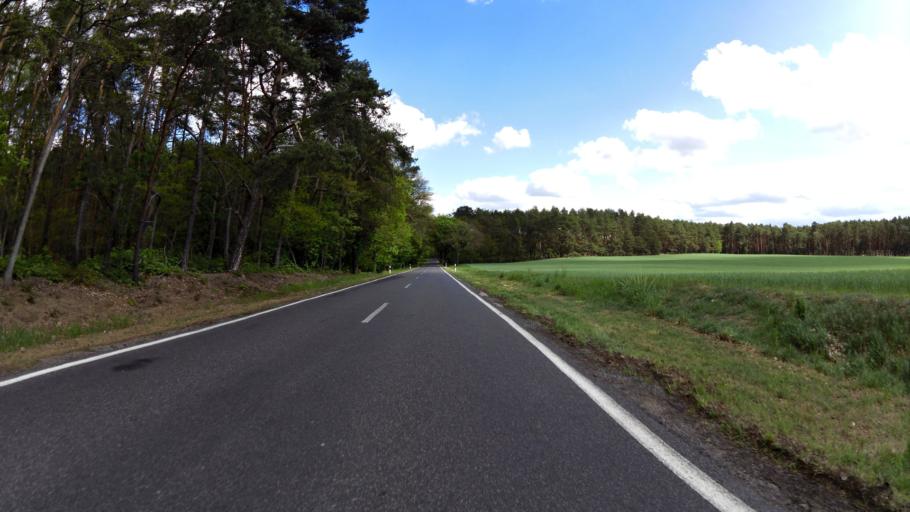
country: DE
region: Brandenburg
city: Wendisch Rietz
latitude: 52.1602
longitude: 14.0290
